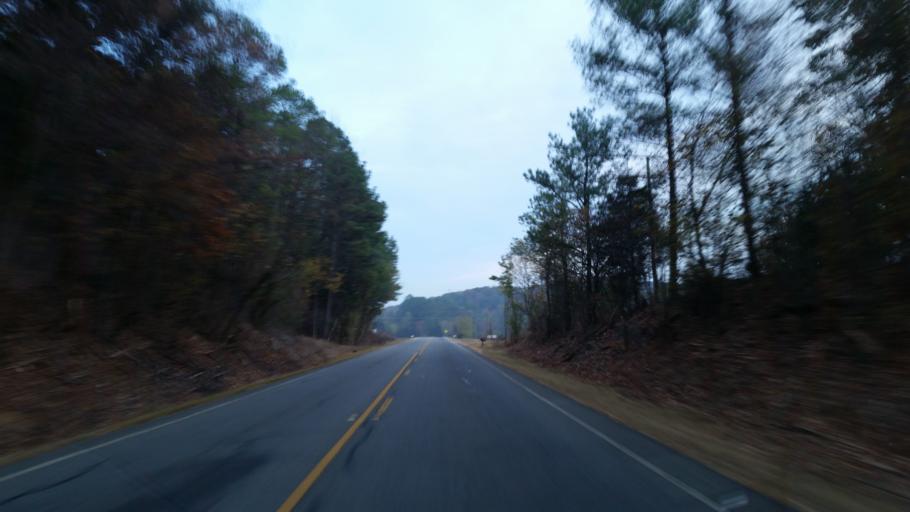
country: US
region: Georgia
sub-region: Murray County
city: Chatsworth
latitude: 34.5898
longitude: -84.7220
